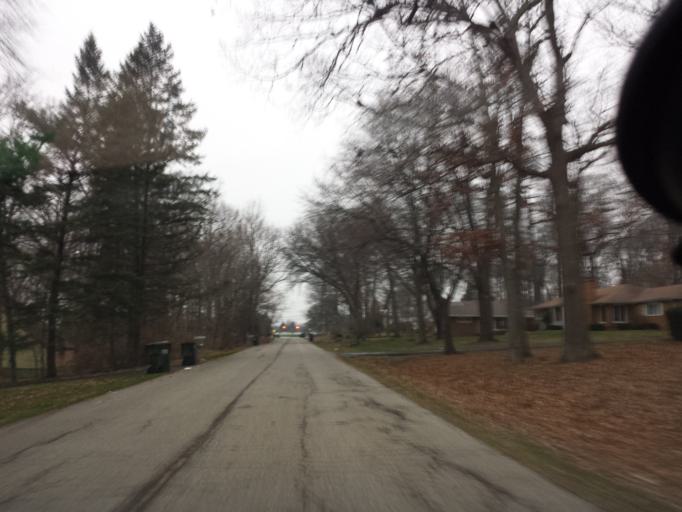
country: US
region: Michigan
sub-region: Oakland County
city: Rochester Hills
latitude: 42.6756
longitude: -83.1907
